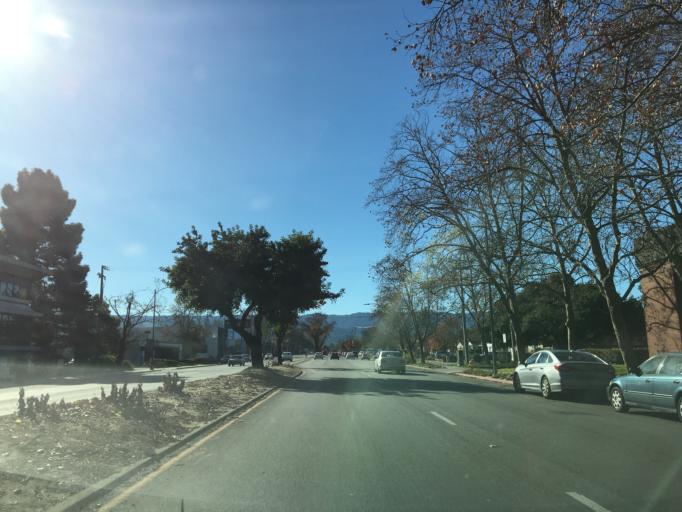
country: US
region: California
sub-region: Santa Clara County
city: Campbell
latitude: 37.2961
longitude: -121.9871
